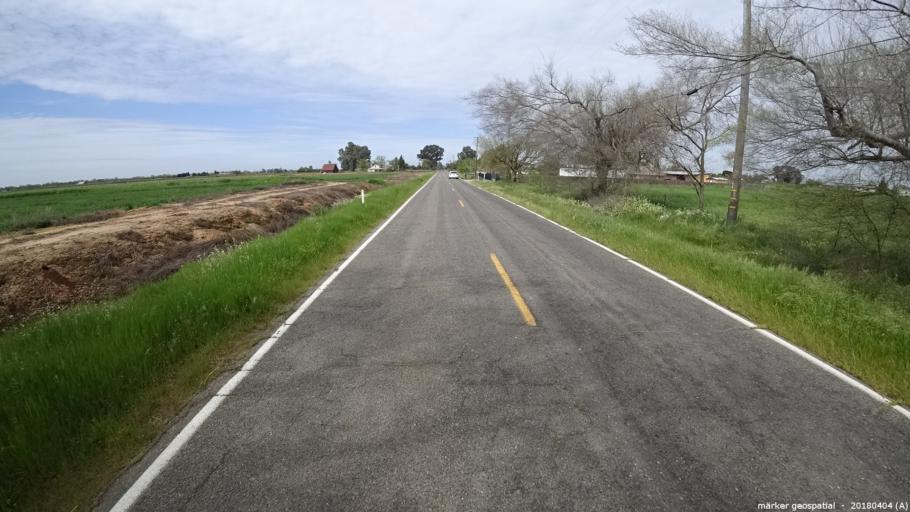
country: US
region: California
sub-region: Sacramento County
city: Herald
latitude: 38.2630
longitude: -121.2304
